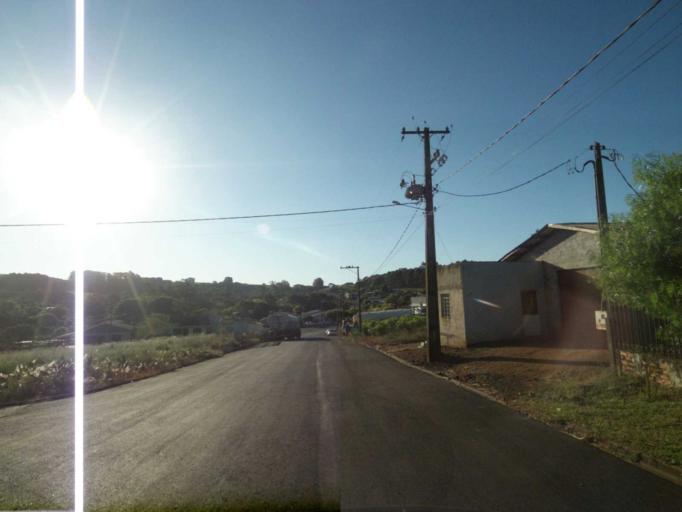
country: BR
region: Parana
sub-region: Coronel Vivida
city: Coronel Vivida
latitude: -25.9767
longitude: -52.8138
